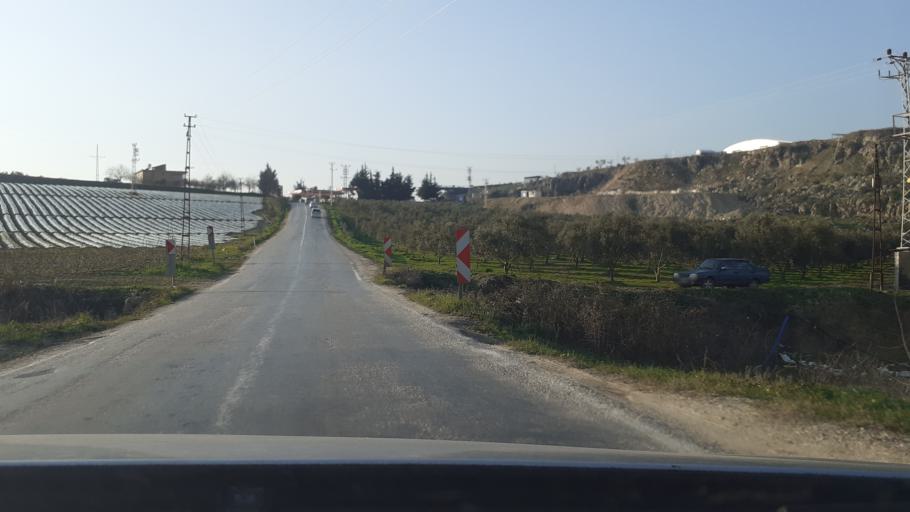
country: TR
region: Hatay
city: Fatikli
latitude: 36.1099
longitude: 36.2711
